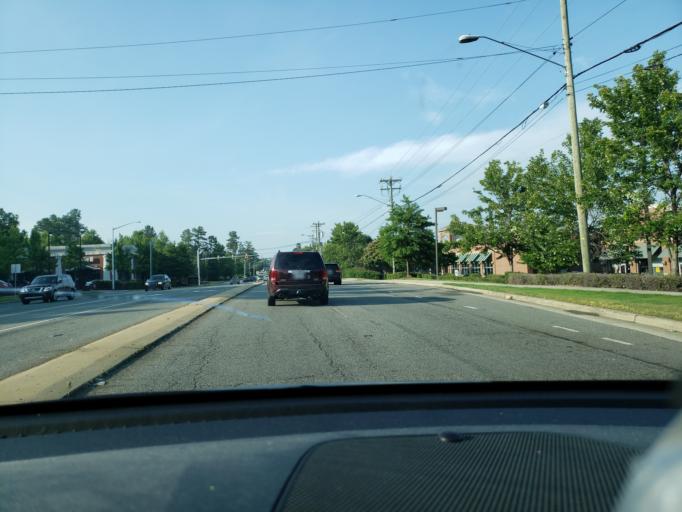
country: US
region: North Carolina
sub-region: Durham County
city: Durham
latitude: 35.9109
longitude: -78.9345
